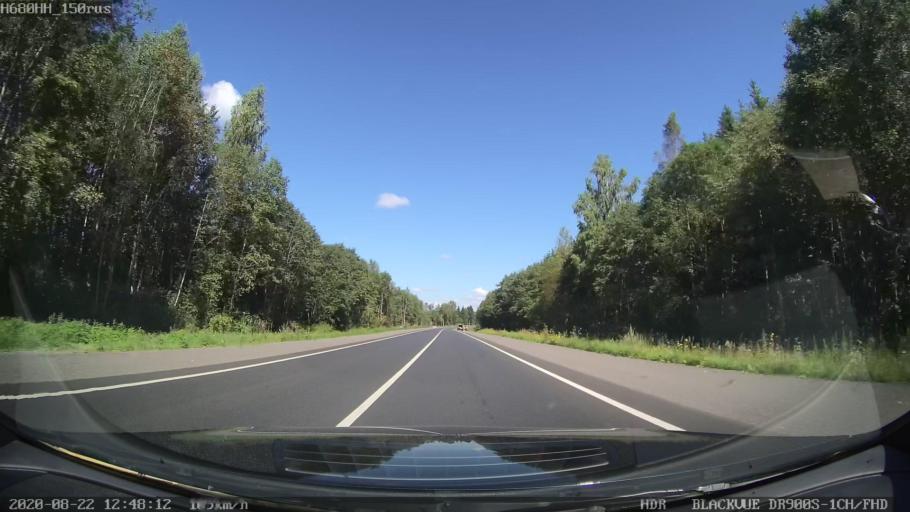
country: RU
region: Tverskaya
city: Rameshki
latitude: 57.4366
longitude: 36.1821
